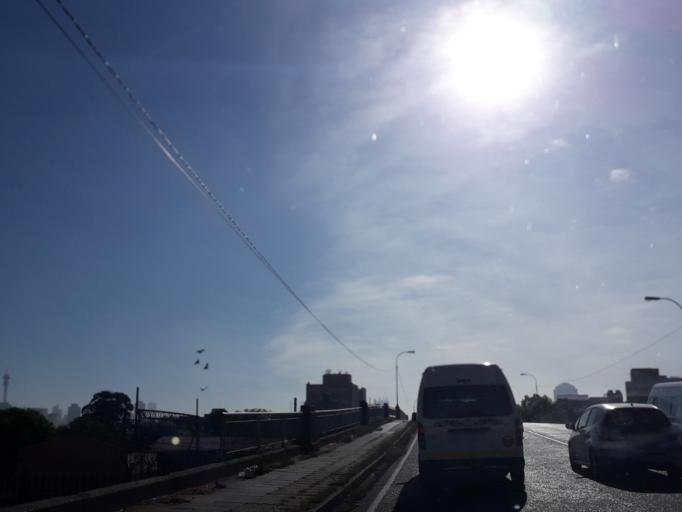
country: ZA
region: Gauteng
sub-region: City of Johannesburg Metropolitan Municipality
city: Johannesburg
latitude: -26.2018
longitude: 28.0178
